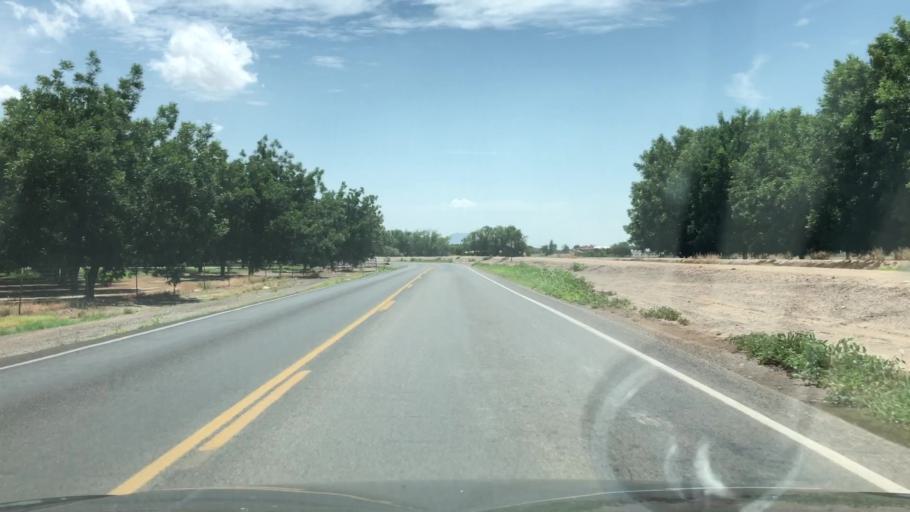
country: US
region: New Mexico
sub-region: Dona Ana County
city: La Union
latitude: 32.0053
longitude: -106.6614
